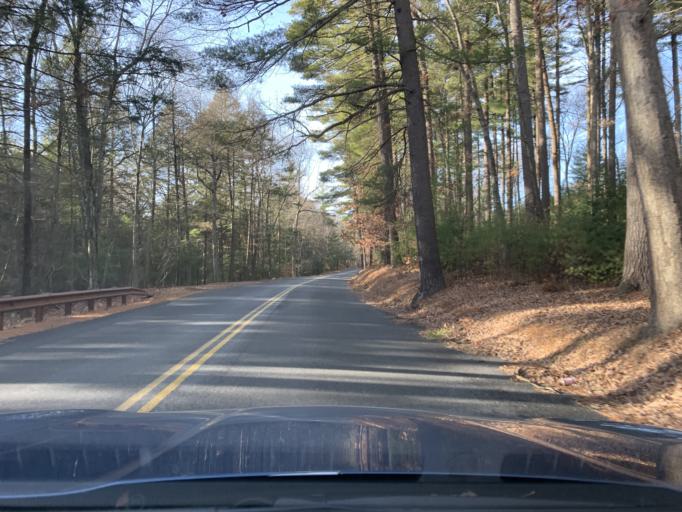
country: US
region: Connecticut
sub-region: Hartford County
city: Weatogue
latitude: 41.8511
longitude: -72.8177
